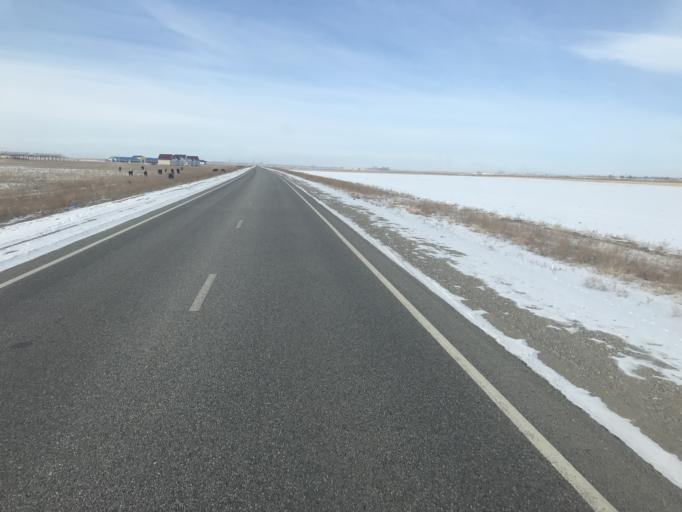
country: KZ
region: Zhambyl
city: Sarykemer
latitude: 43.0510
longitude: 71.4762
